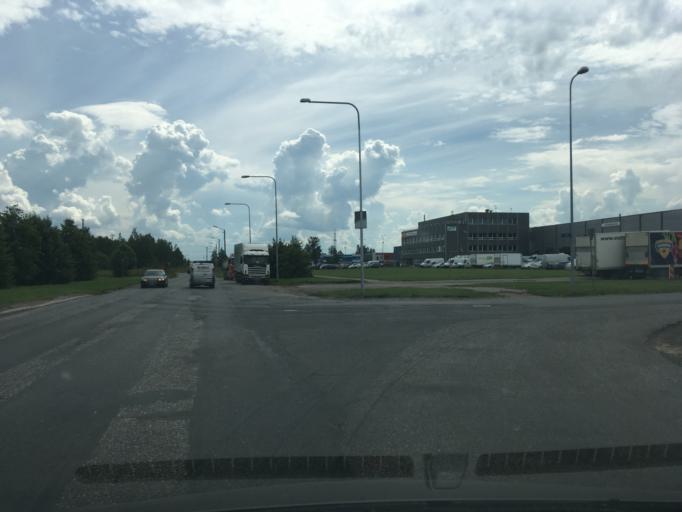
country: EE
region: Harju
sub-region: Tallinna linn
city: Kose
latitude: 59.4277
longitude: 24.8498
